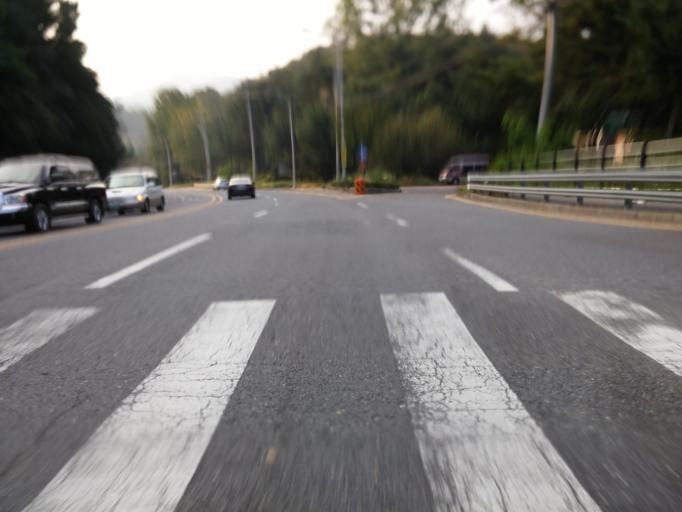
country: KR
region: Daejeon
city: Daejeon
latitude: 36.3473
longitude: 127.4972
